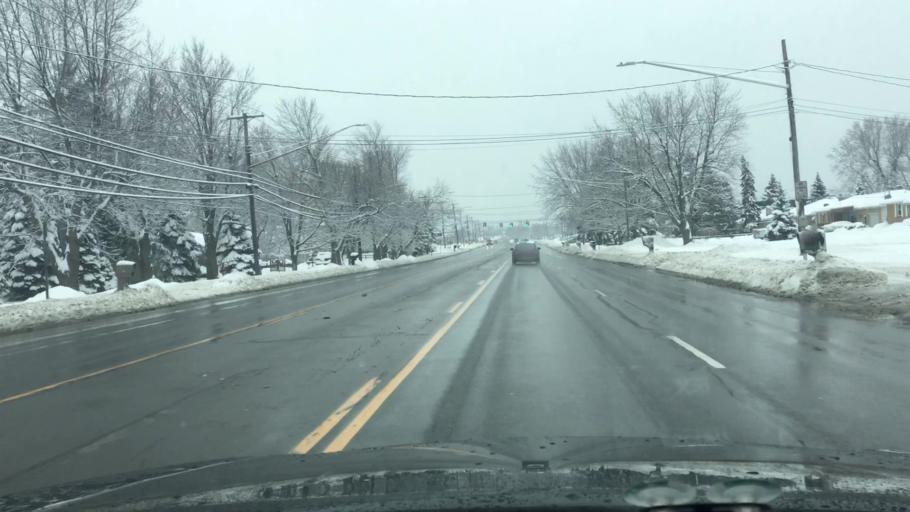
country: US
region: New York
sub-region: Erie County
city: Orchard Park
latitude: 42.8058
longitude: -78.7519
